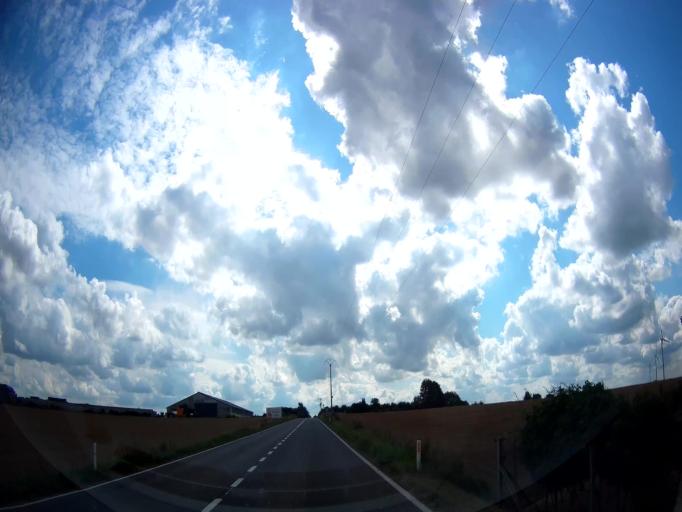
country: BE
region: Wallonia
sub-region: Province de Namur
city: Ohey
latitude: 50.4155
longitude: 5.1231
